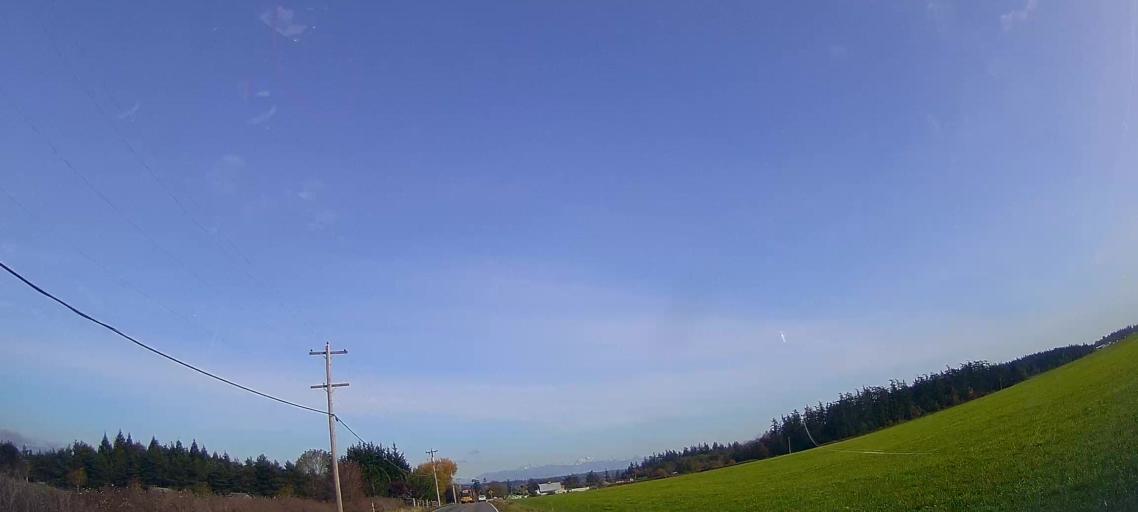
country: US
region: Washington
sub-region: Snohomish County
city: Stanwood
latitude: 48.2544
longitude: -122.4327
